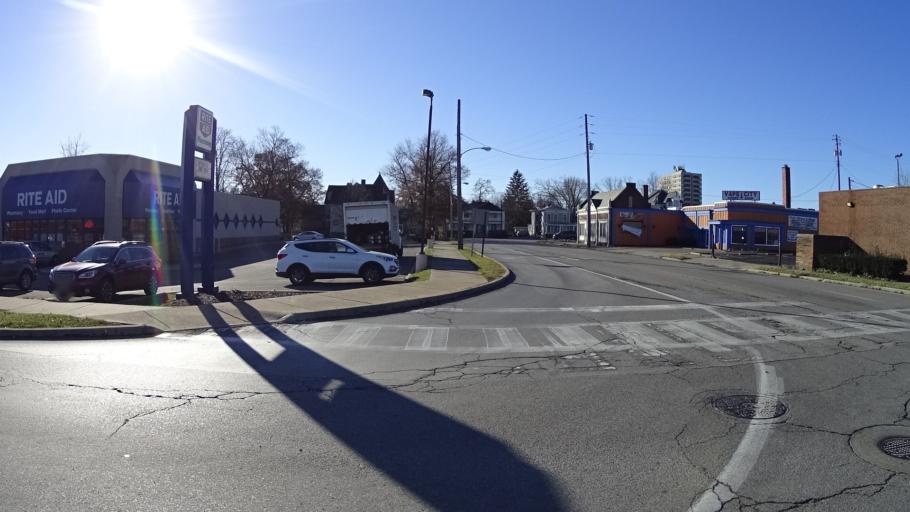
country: US
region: Ohio
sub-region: Lorain County
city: Elyria
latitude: 41.3675
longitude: -82.1019
